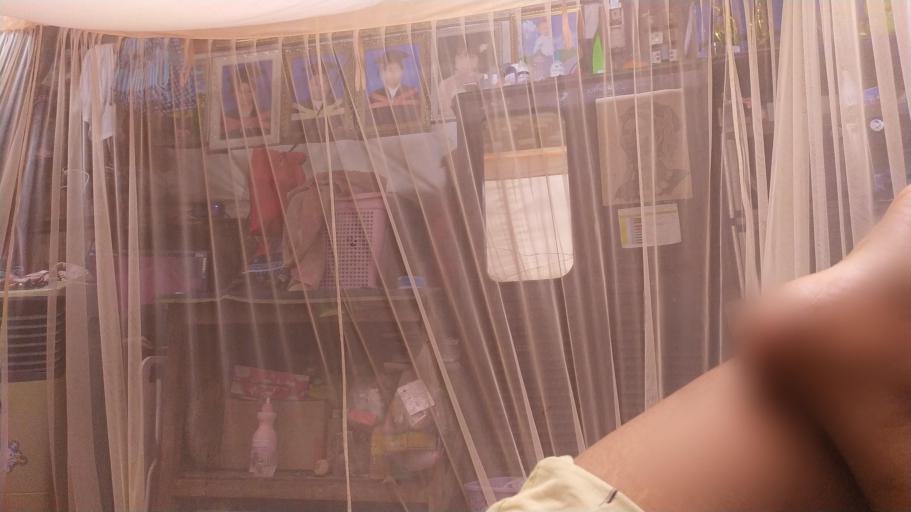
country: MM
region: Mandalay
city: Mandalay
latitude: 21.9202
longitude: 96.0672
